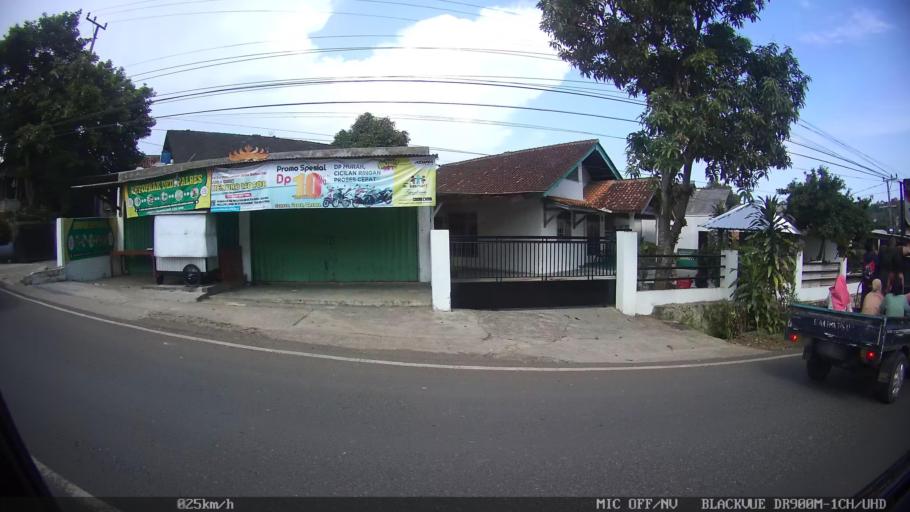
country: ID
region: Lampung
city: Bandarlampung
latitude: -5.4031
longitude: 105.2122
